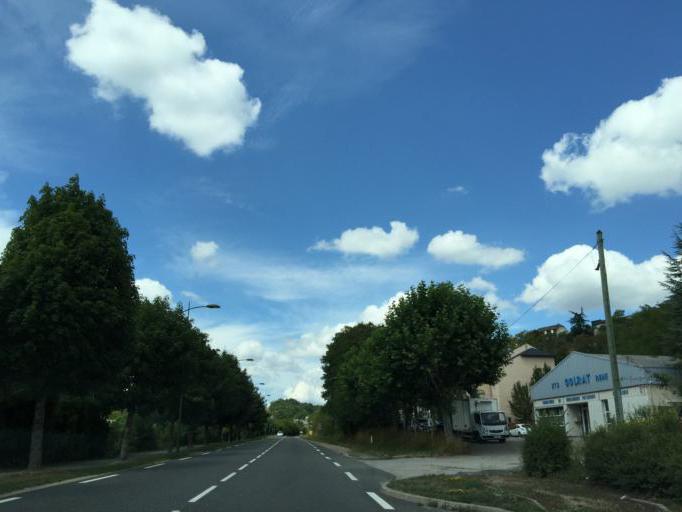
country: FR
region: Midi-Pyrenees
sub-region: Departement de l'Aveyron
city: Rodez
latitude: 44.3730
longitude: 2.5672
